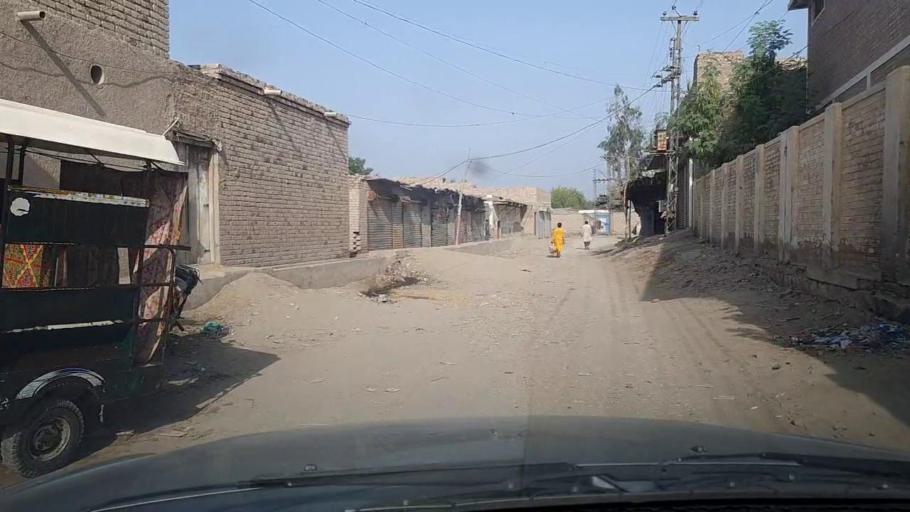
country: PK
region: Sindh
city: Pir jo Goth
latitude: 27.5559
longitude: 68.5519
